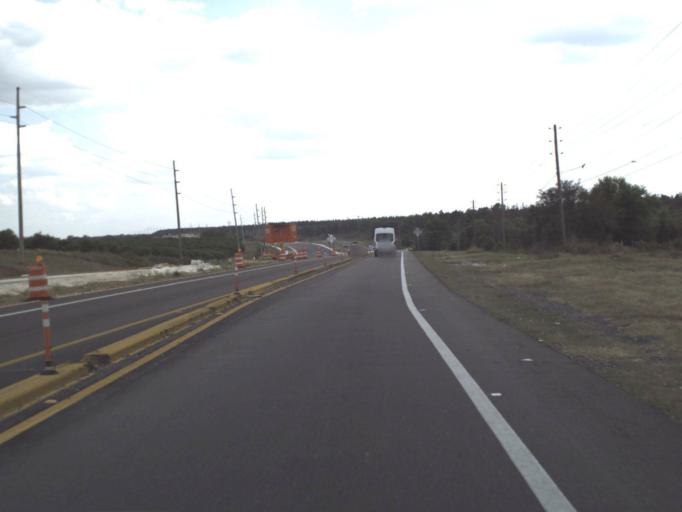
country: US
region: Florida
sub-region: Lake County
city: Clermont
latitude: 28.4553
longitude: -81.7207
